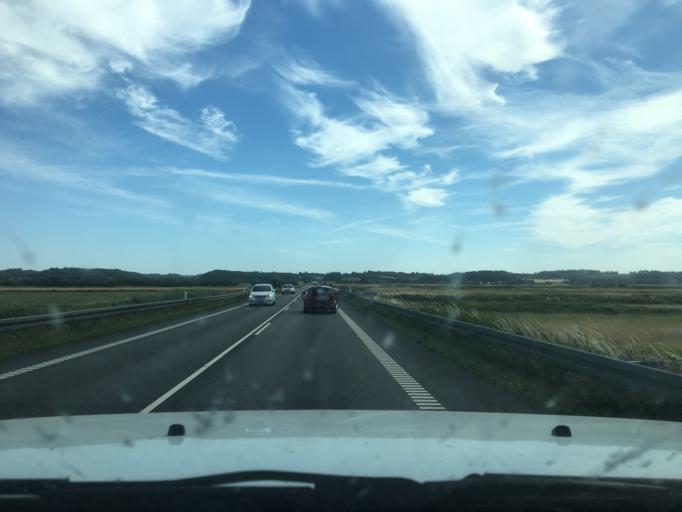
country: DK
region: Central Jutland
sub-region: Viborg Kommune
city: Viborg
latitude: 56.5425
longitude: 9.4022
